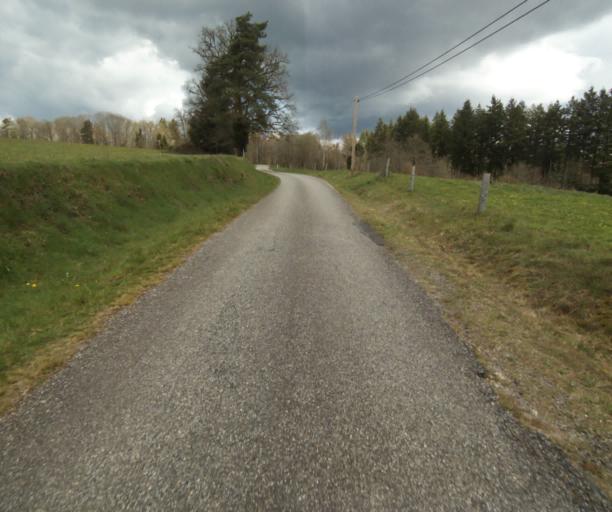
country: FR
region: Limousin
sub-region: Departement de la Correze
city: Laguenne
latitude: 45.2365
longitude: 1.8978
